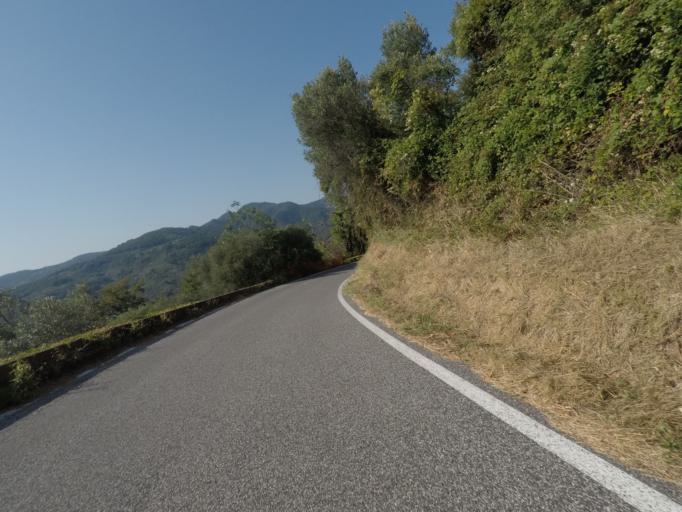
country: IT
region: Liguria
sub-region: Provincia di La Spezia
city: Casano-Dogana-Isola
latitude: 44.0816
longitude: 10.0490
